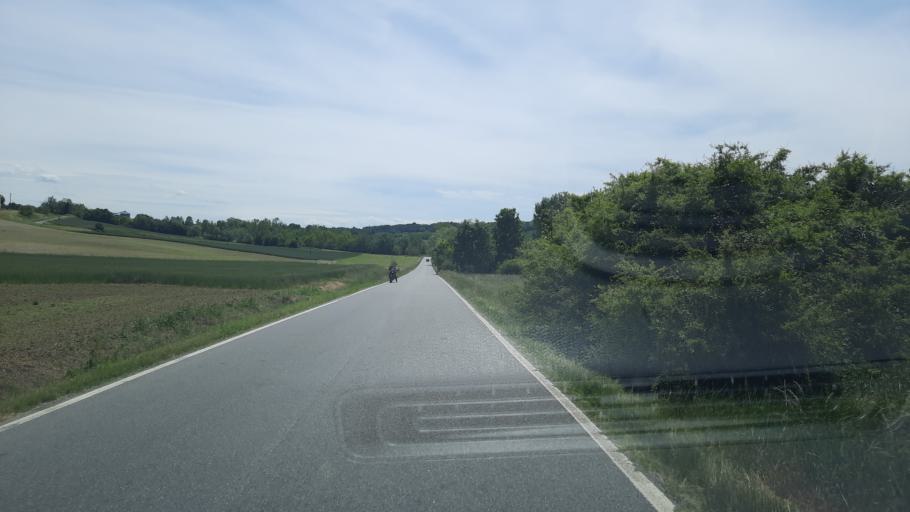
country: IT
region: Piedmont
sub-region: Provincia di Alessandria
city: Castelletto Merli
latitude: 45.0593
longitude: 8.2367
